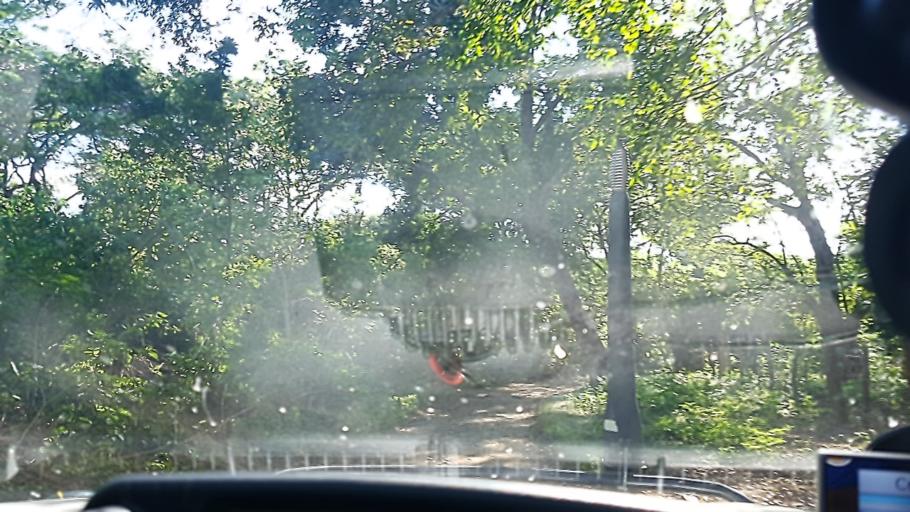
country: NI
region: Rivas
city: Tola
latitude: 11.5402
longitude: -86.1223
